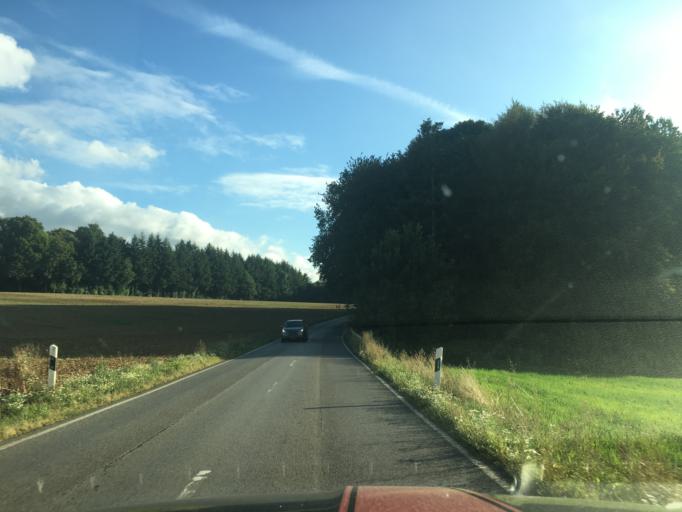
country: FR
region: Lorraine
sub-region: Departement de Meurthe-et-Moselle
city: Hussigny-Godbrange
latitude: 49.5077
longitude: 5.8701
